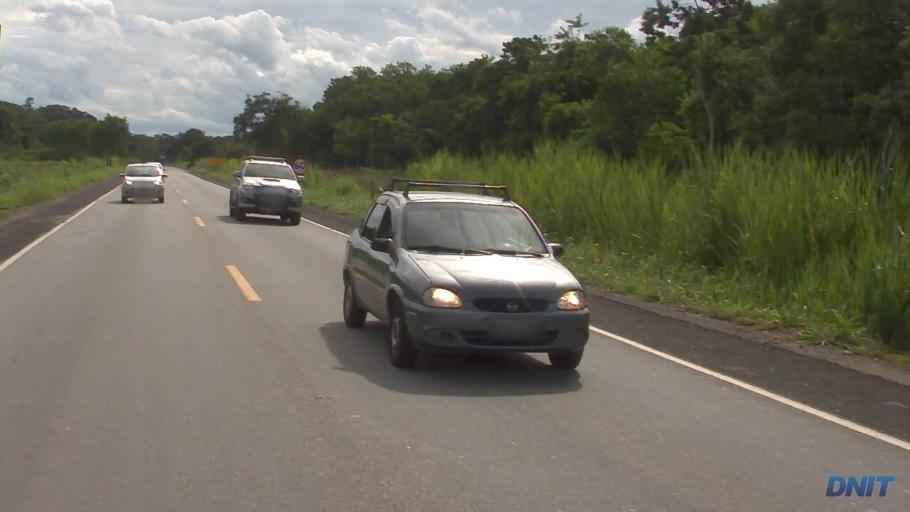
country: BR
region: Minas Gerais
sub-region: Ipaba
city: Ipaba
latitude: -19.2987
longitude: -42.3715
